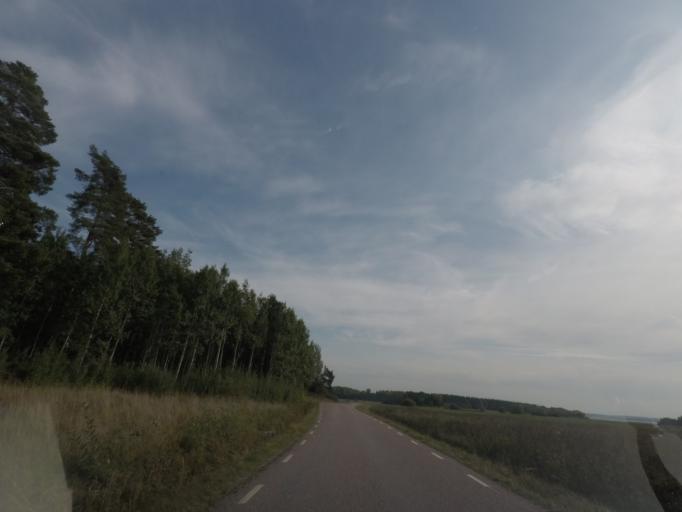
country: SE
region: Vaestmanland
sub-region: Kungsors Kommun
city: Kungsoer
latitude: 59.4937
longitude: 16.1545
